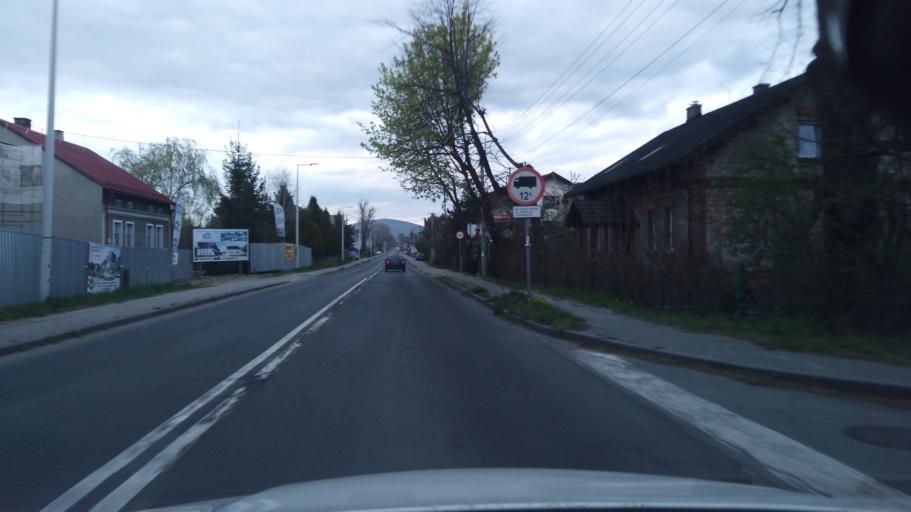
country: PL
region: Silesian Voivodeship
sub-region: Powiat zywiecki
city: Wieprz
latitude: 49.6665
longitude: 19.1776
